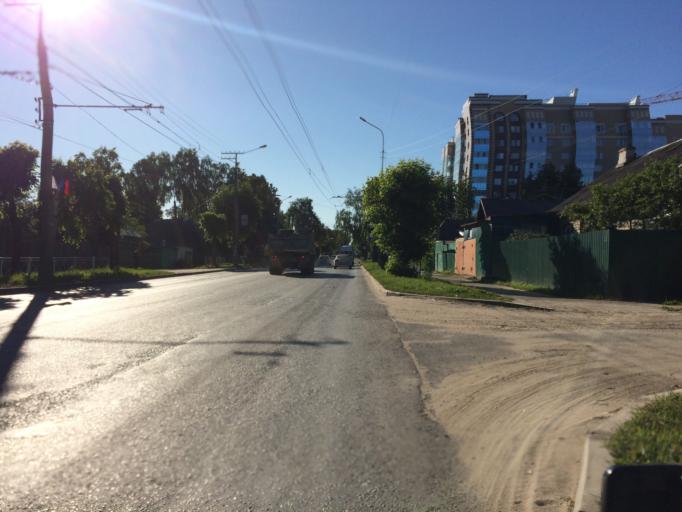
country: RU
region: Mariy-El
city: Yoshkar-Ola
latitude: 56.6505
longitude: 47.8936
